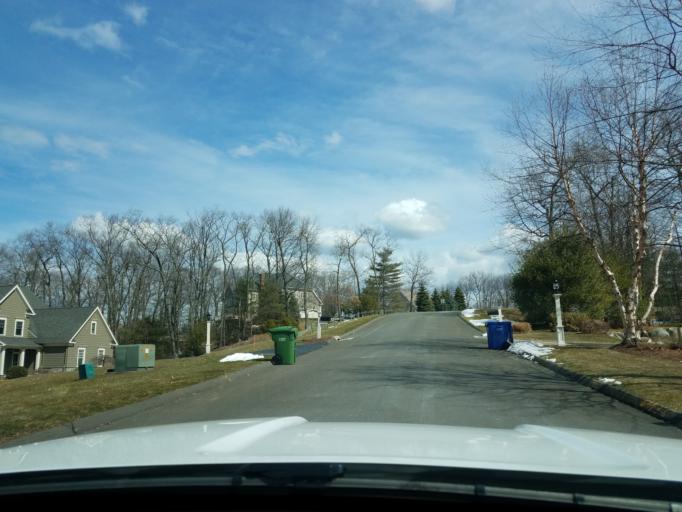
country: US
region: Connecticut
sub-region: Hartford County
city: Collinsville
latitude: 41.7897
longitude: -72.9036
